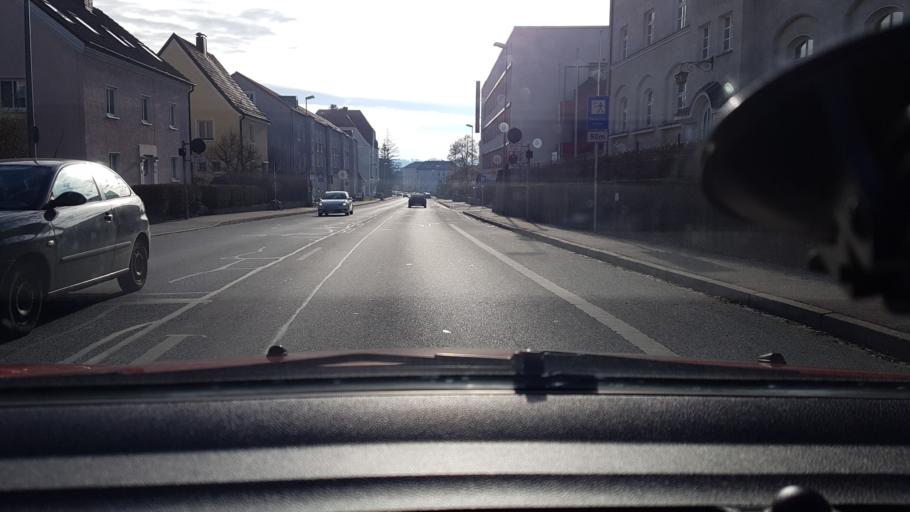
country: DE
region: Bavaria
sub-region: Lower Bavaria
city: Pfarrkirchen
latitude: 48.4368
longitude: 12.9370
